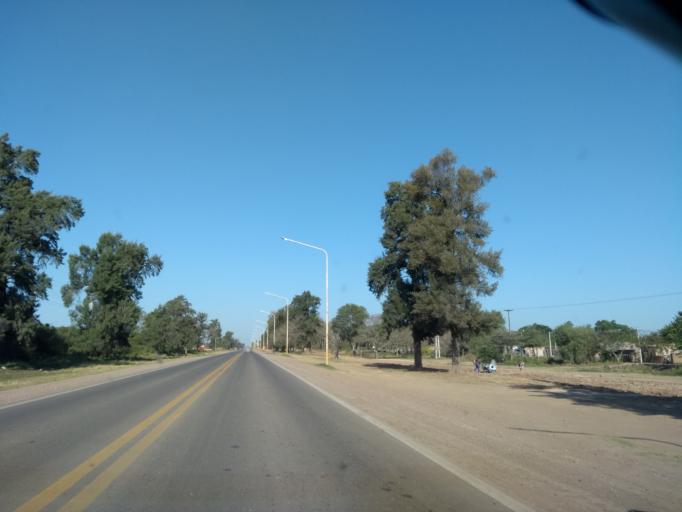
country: AR
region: Chaco
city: Presidencia Roque Saenz Pena
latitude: -26.7920
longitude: -60.4094
